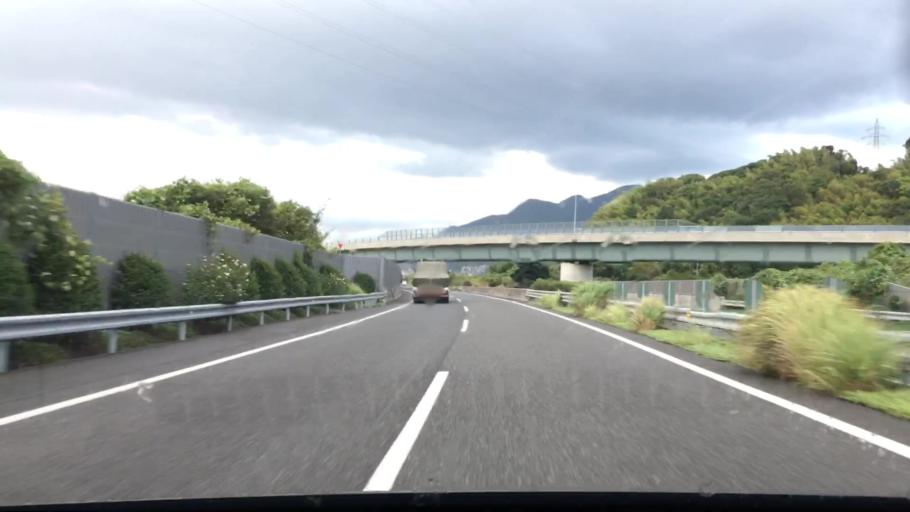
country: JP
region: Fukuoka
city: Kitakyushu
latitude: 33.8157
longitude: 130.8846
